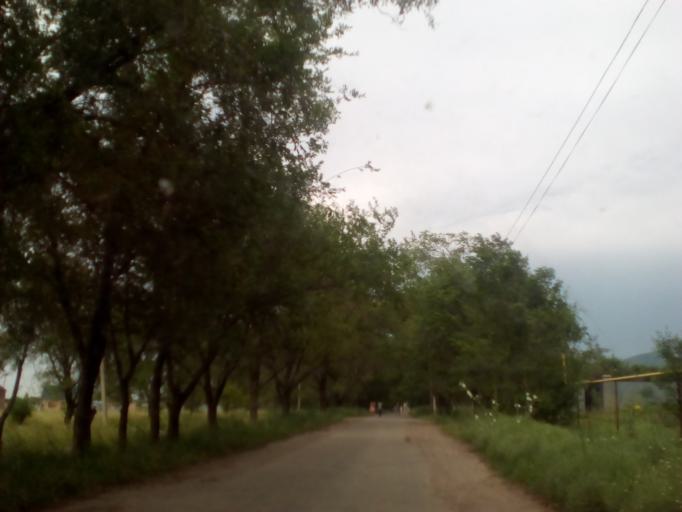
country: KZ
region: Almaty Oblysy
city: Burunday
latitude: 43.1593
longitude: 76.3941
